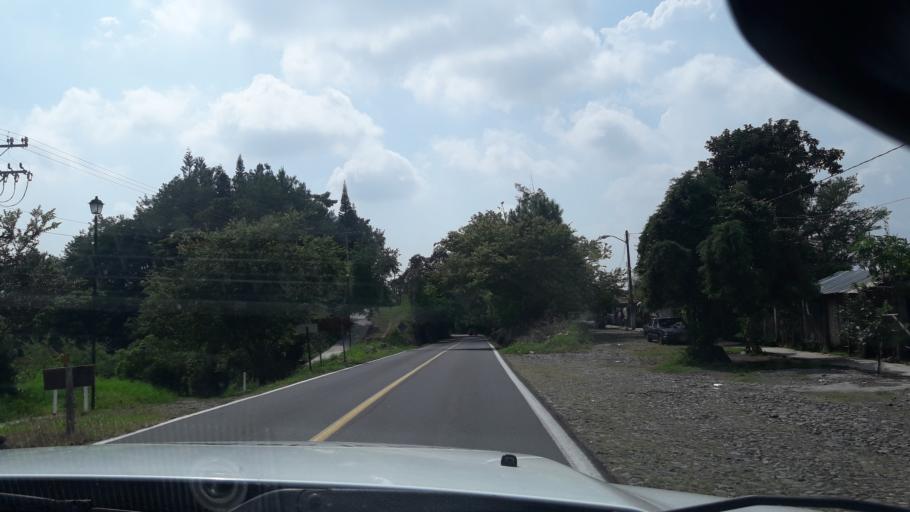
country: MX
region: Colima
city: Suchitlan
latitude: 19.3910
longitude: -103.7065
